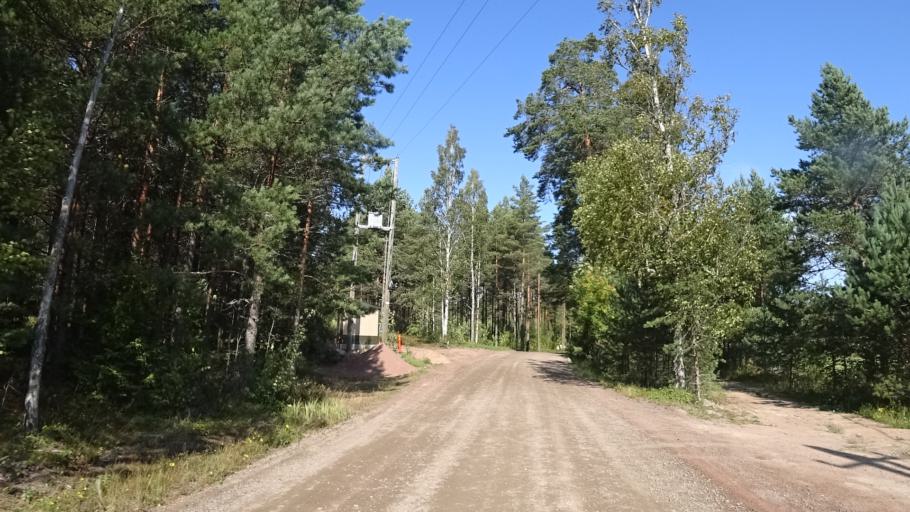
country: FI
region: Kymenlaakso
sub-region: Kotka-Hamina
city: Hamina
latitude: 60.5443
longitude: 27.2185
